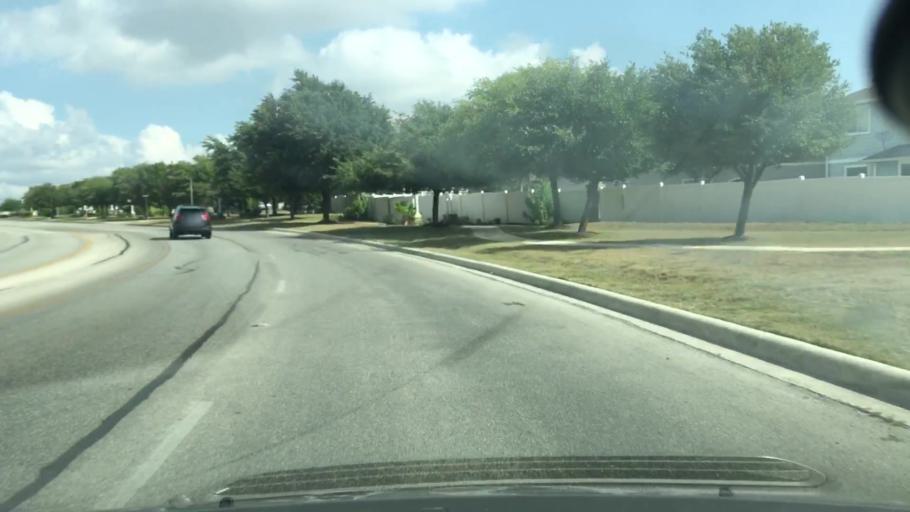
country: US
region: Texas
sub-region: Guadalupe County
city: Cibolo
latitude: 29.5903
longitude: -98.2491
